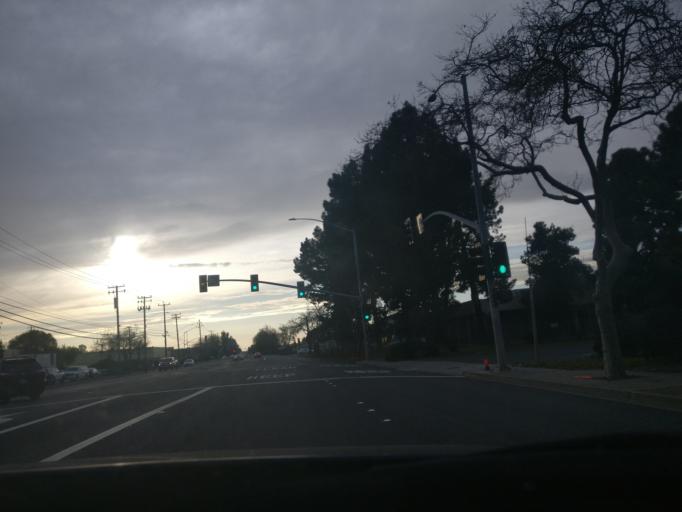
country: US
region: California
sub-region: Alameda County
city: San Lorenzo
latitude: 37.6532
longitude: -122.1184
